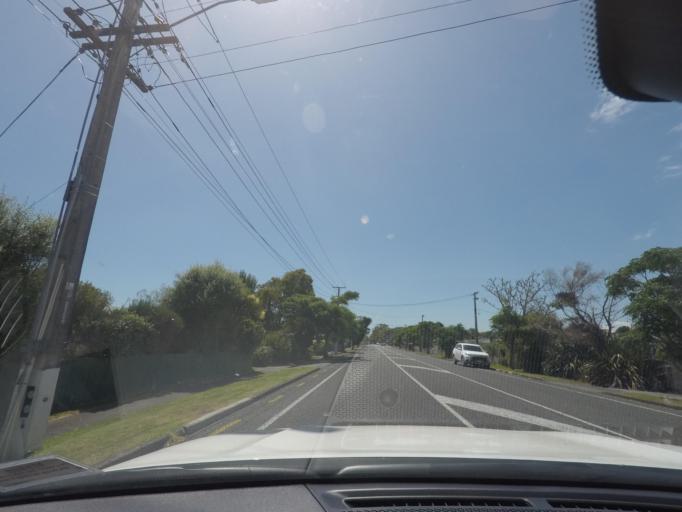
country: NZ
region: Auckland
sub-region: Auckland
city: Parakai
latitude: -36.6629
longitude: 174.4355
